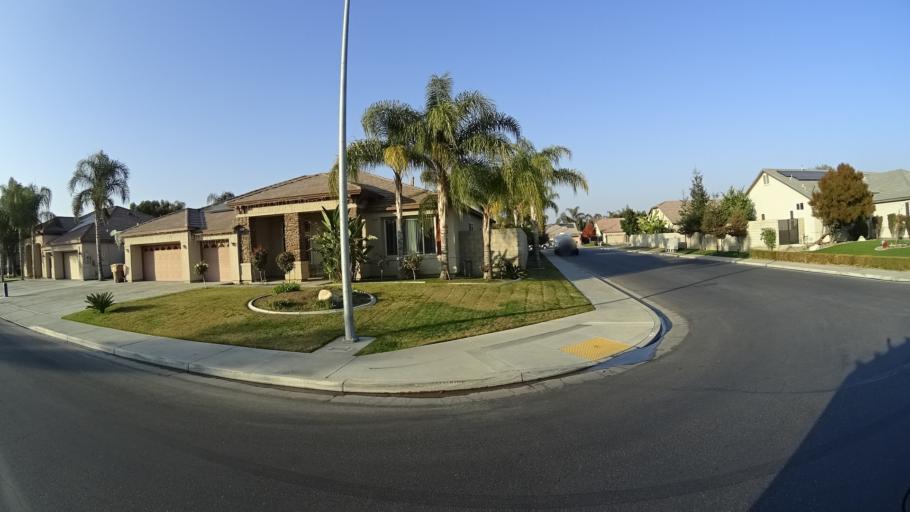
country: US
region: California
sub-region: Kern County
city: Rosedale
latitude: 35.3798
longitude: -119.1497
